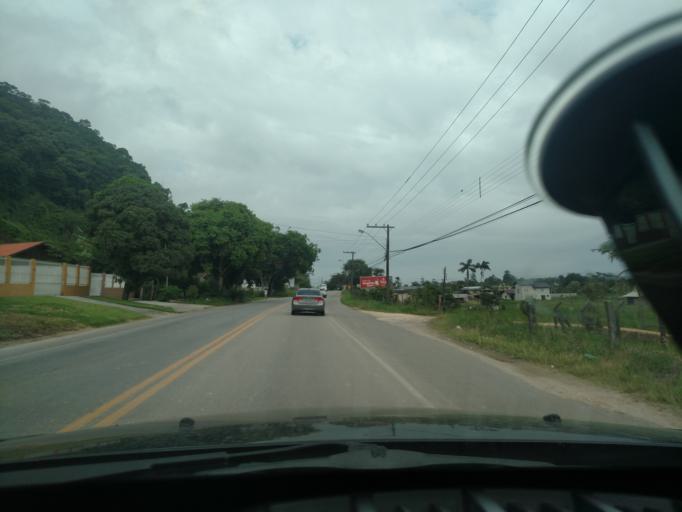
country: BR
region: Santa Catarina
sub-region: Itajai
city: Itajai
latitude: -26.8866
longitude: -48.7498
